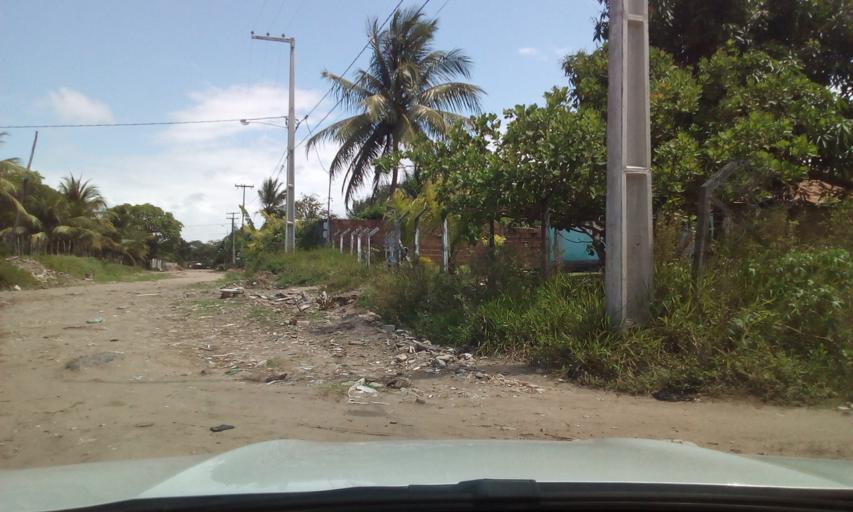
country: BR
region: Paraiba
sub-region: Joao Pessoa
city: Joao Pessoa
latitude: -7.1478
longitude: -34.8065
